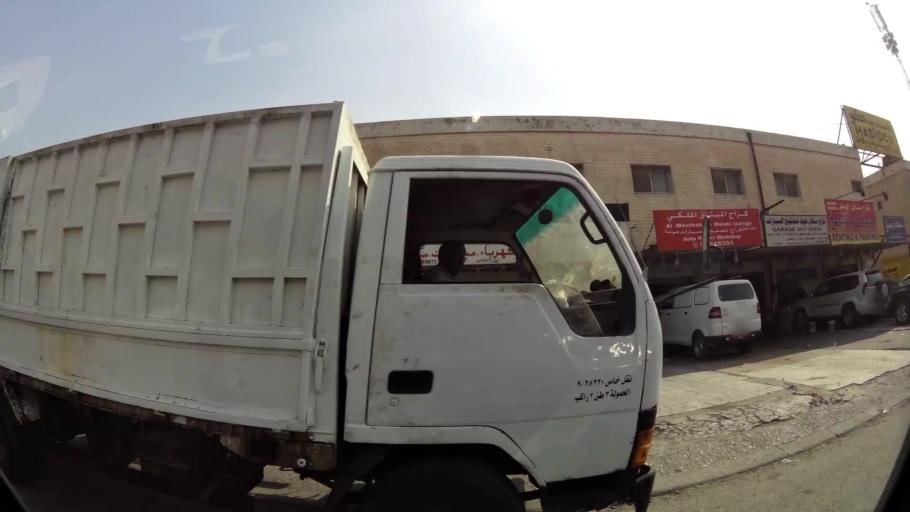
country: KW
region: Al Asimah
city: Ash Shamiyah
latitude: 29.3317
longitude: 47.9457
